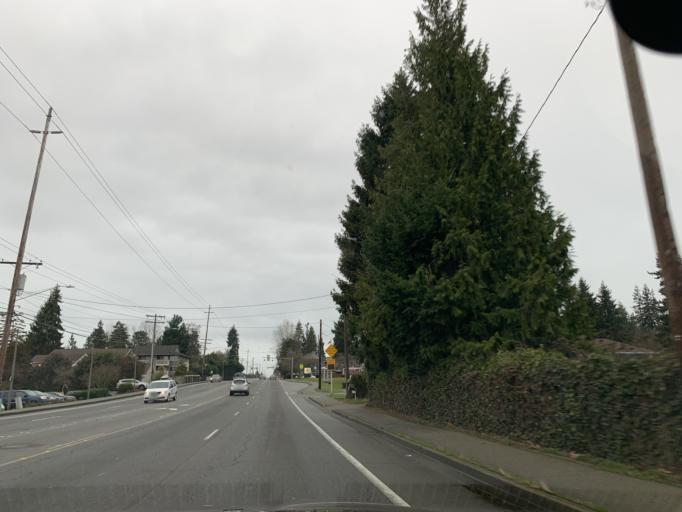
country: US
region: Washington
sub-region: Snohomish County
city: Everett
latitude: 47.9220
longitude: -122.2318
